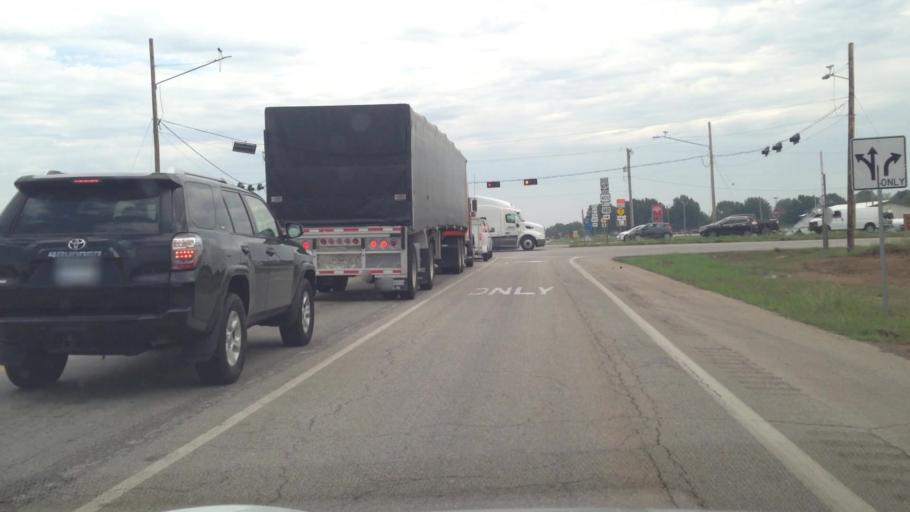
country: US
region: Kansas
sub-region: Crawford County
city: Pittsburg
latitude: 37.3386
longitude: -94.7063
